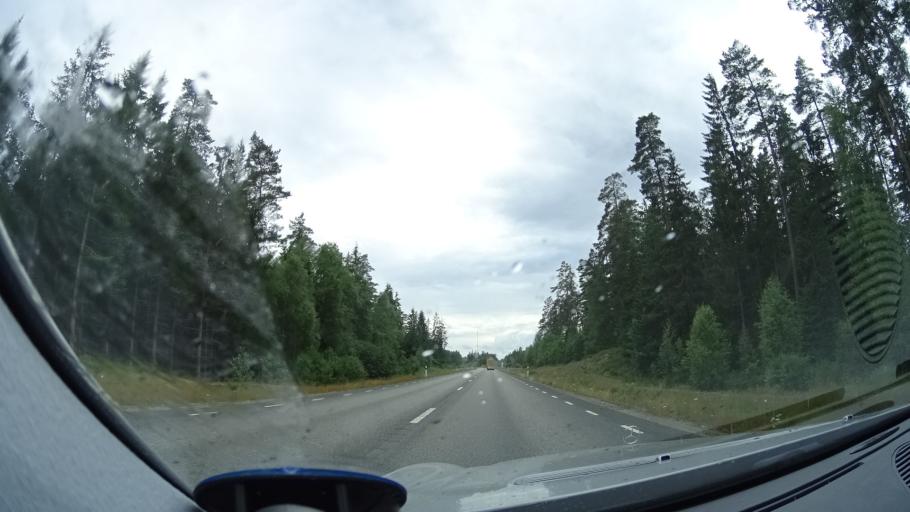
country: SE
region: Kronoberg
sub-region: Tingsryds Kommun
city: Tingsryd
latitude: 56.3935
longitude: 14.9129
